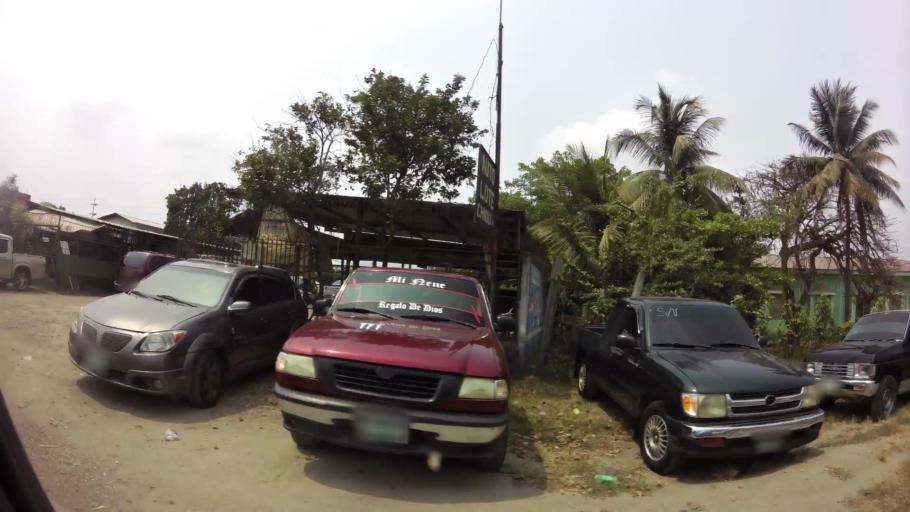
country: HN
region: Yoro
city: El Progreso
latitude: 15.4030
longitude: -87.8160
